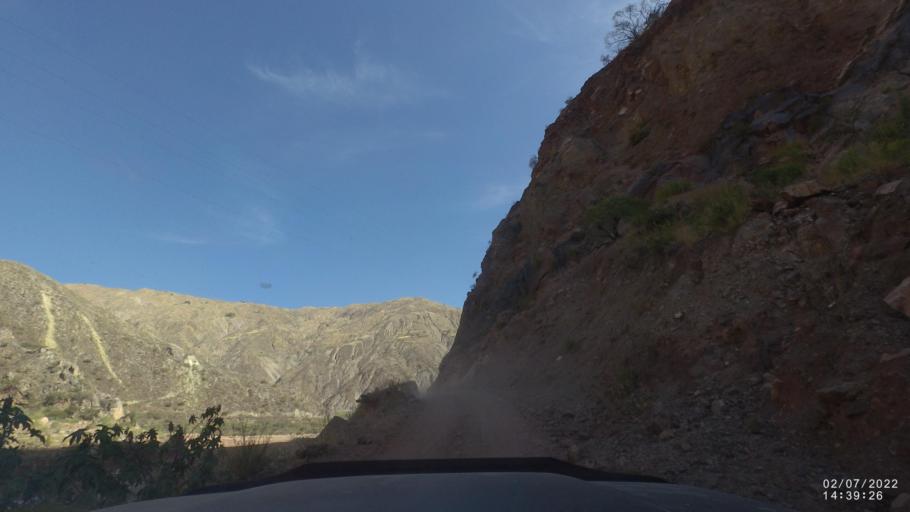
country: BO
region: Cochabamba
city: Irpa Irpa
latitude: -17.8472
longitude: -66.4194
